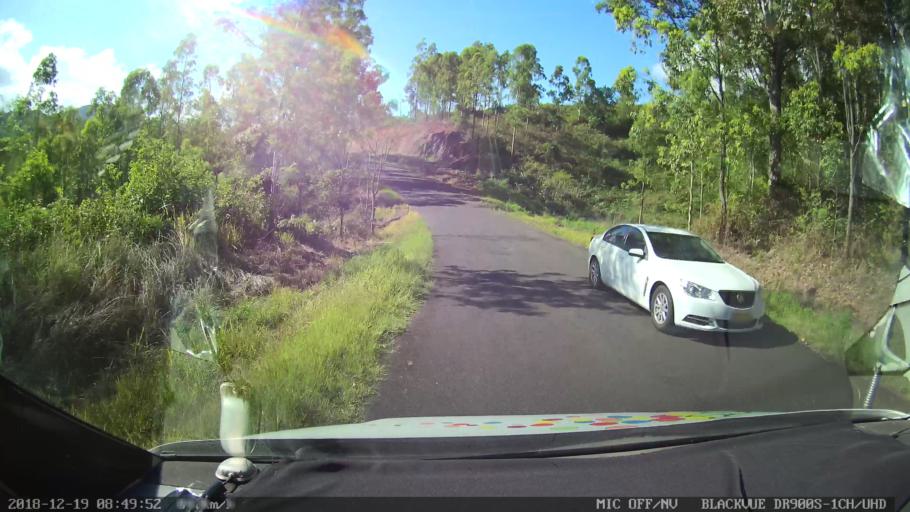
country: AU
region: New South Wales
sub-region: Kyogle
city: Kyogle
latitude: -28.3779
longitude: 152.9732
